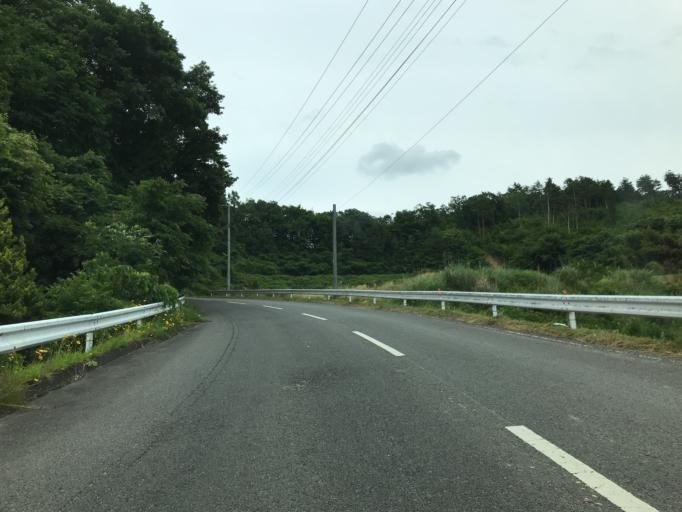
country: JP
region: Fukushima
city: Funehikimachi-funehiki
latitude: 37.3865
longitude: 140.5405
